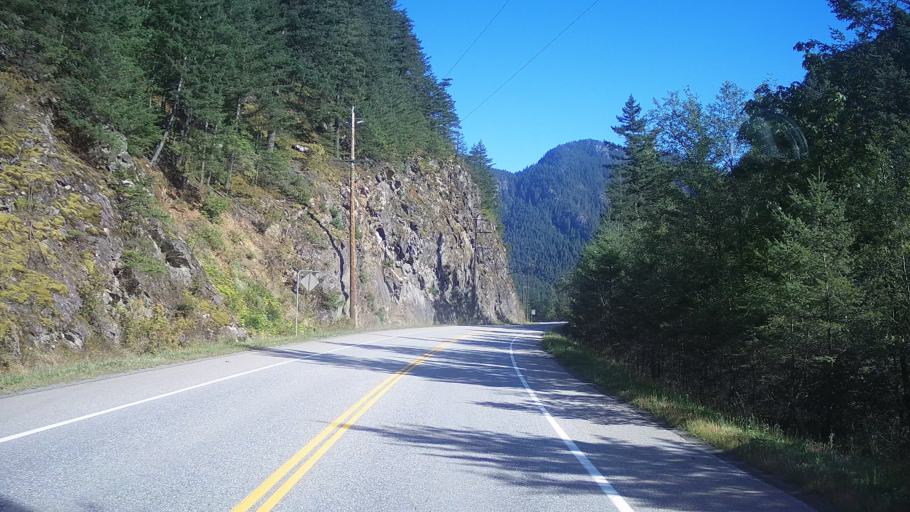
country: CA
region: British Columbia
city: Hope
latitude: 49.5920
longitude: -121.4097
